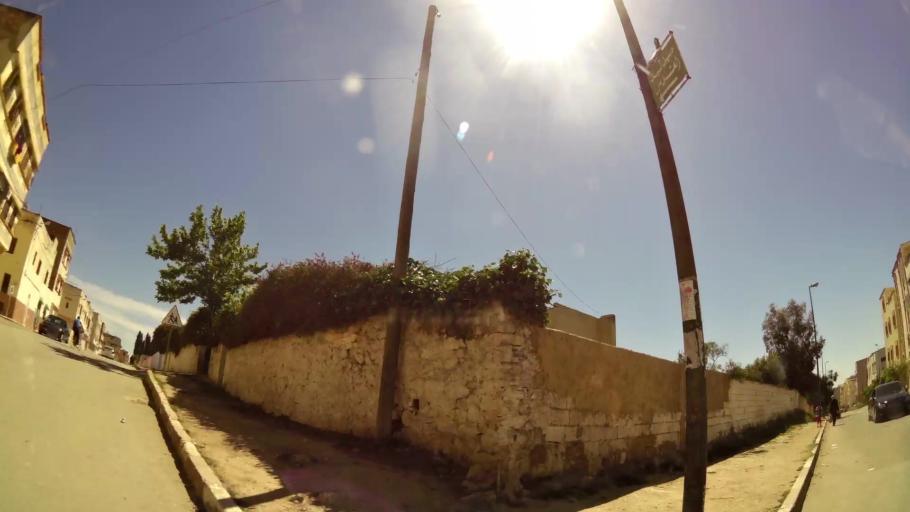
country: MA
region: Meknes-Tafilalet
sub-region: Meknes
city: Meknes
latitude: 33.8894
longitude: -5.5730
